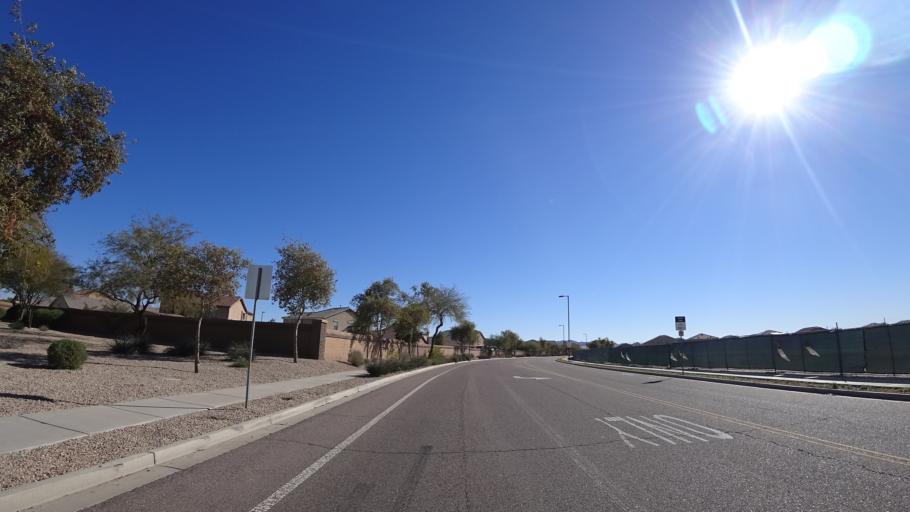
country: US
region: Arizona
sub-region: Maricopa County
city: Goodyear
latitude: 33.4209
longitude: -112.4067
